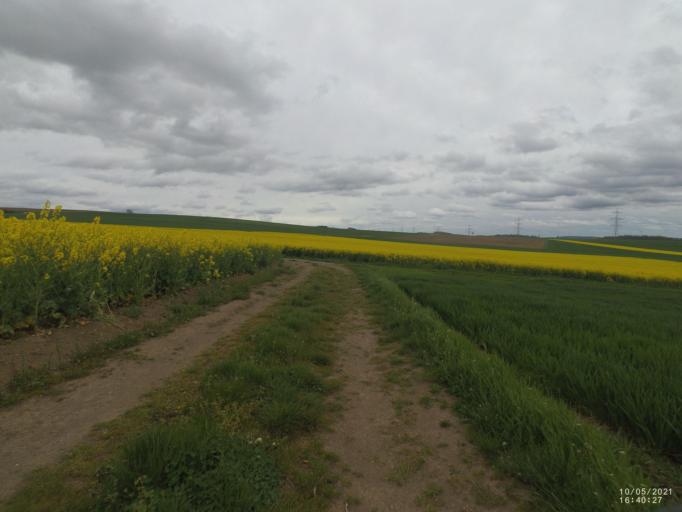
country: DE
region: Rheinland-Pfalz
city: Kerben
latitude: 50.3112
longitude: 7.3826
